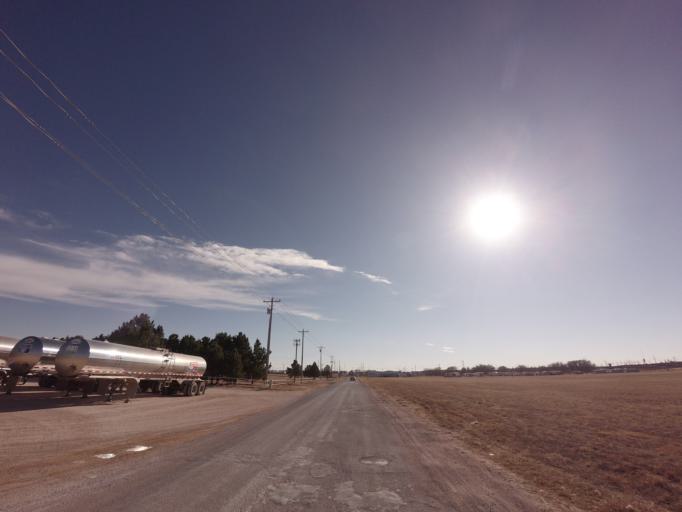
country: US
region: New Mexico
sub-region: Curry County
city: Clovis
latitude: 34.4008
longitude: -103.1612
